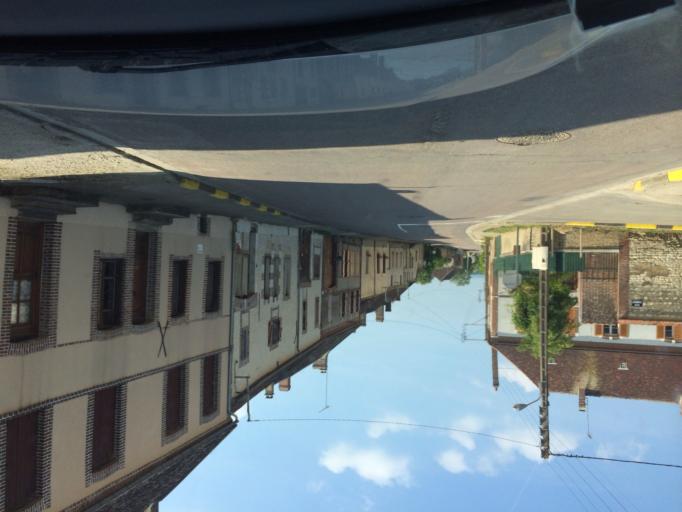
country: FR
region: Bourgogne
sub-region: Departement de l'Yonne
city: Fleury-la-Vallee
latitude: 47.9174
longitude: 3.4392
